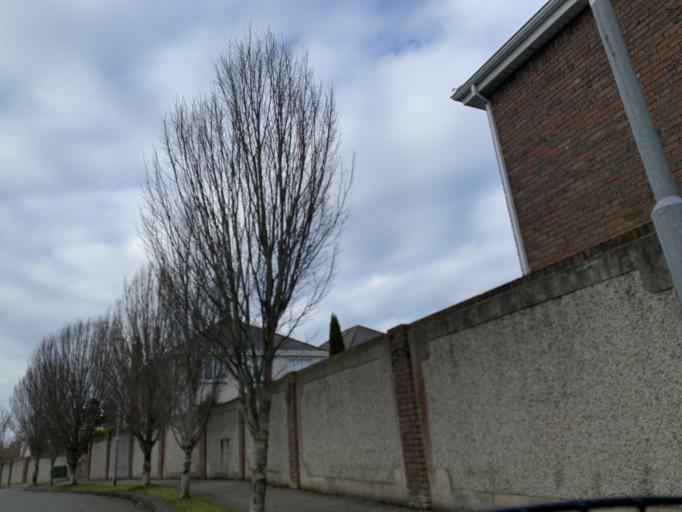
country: IE
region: Leinster
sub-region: Kildare
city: Celbridge
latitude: 53.3304
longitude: -6.5463
